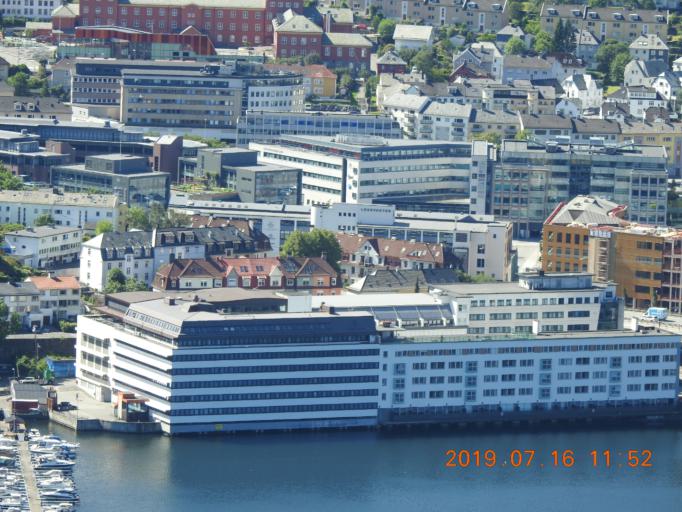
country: NO
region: Hordaland
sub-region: Bergen
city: Bergen
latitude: 60.3908
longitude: 5.3492
